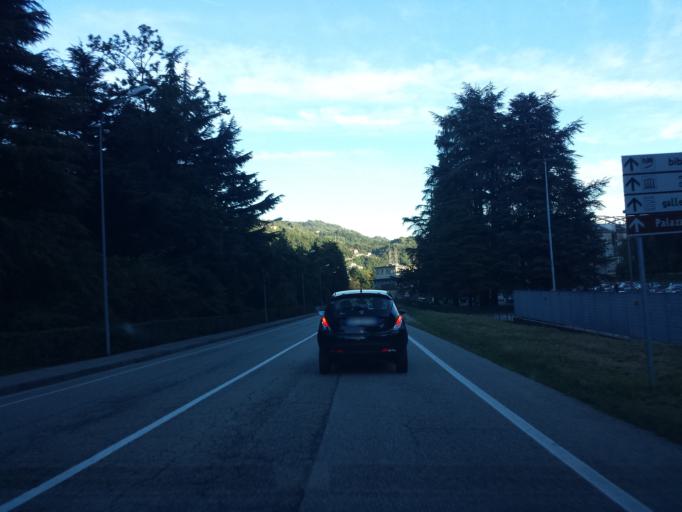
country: IT
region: Veneto
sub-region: Provincia di Vicenza
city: Valdagno
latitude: 45.6567
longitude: 11.2977
